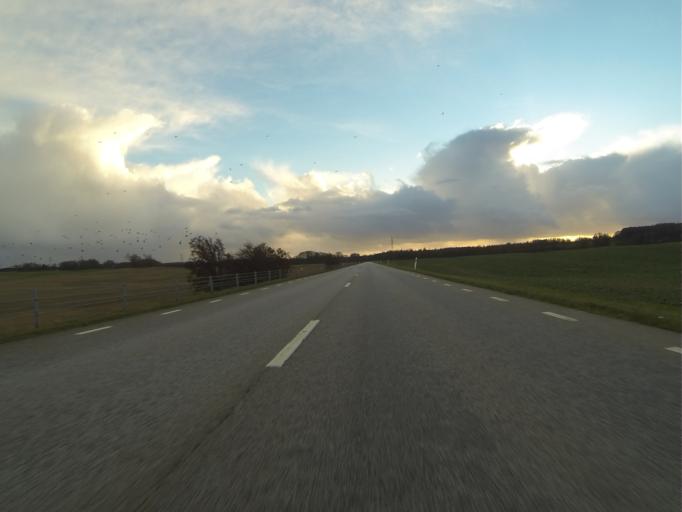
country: SE
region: Skane
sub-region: Trelleborgs Kommun
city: Anderslov
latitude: 55.5167
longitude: 13.3309
